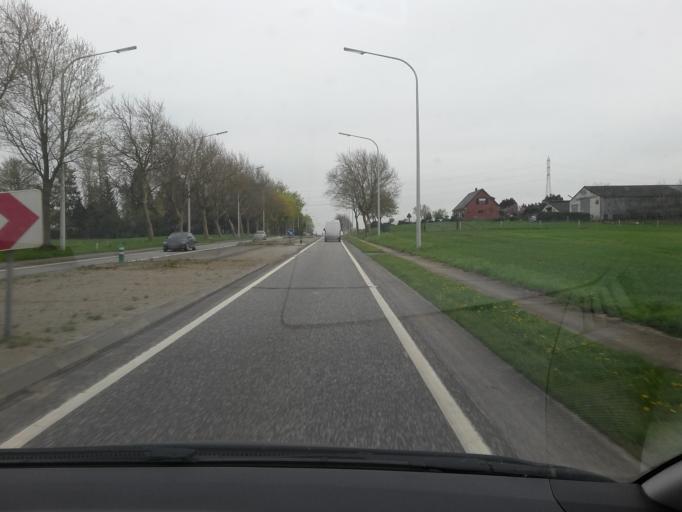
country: BE
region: Wallonia
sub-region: Province du Brabant Wallon
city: Genappe
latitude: 50.6357
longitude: 4.4274
